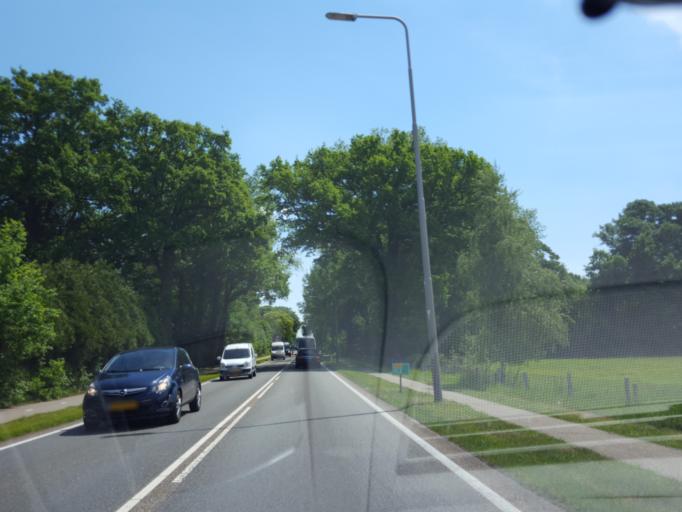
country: NL
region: Limburg
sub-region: Gemeente Leudal
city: Heythuysen
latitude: 51.2180
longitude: 5.8899
